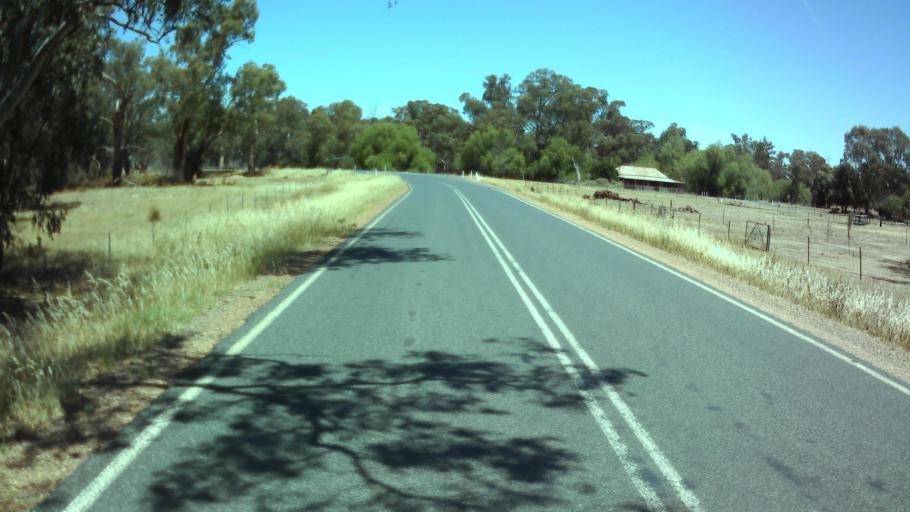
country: AU
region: New South Wales
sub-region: Weddin
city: Grenfell
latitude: -34.0387
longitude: 147.9305
